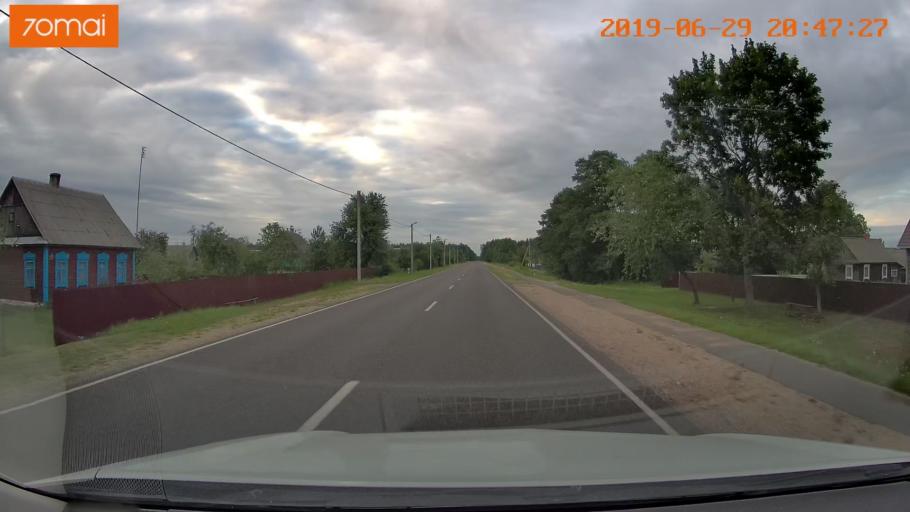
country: BY
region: Brest
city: Hantsavichy
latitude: 52.6386
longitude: 26.3155
